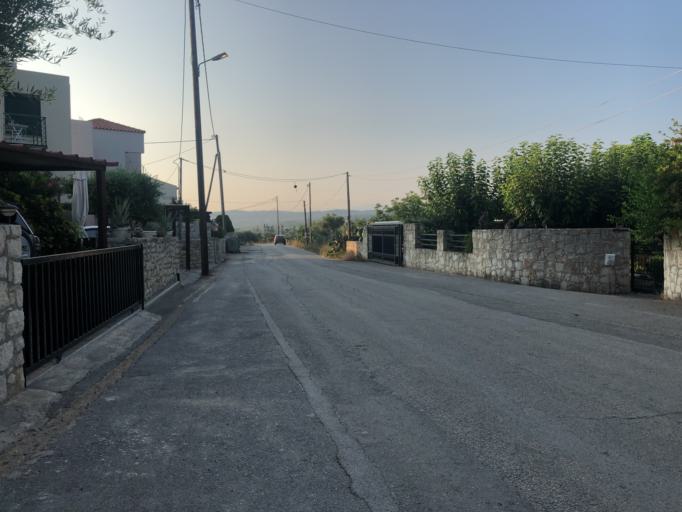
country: GR
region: Crete
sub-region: Nomos Chanias
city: Georgioupolis
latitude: 35.3485
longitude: 24.2850
